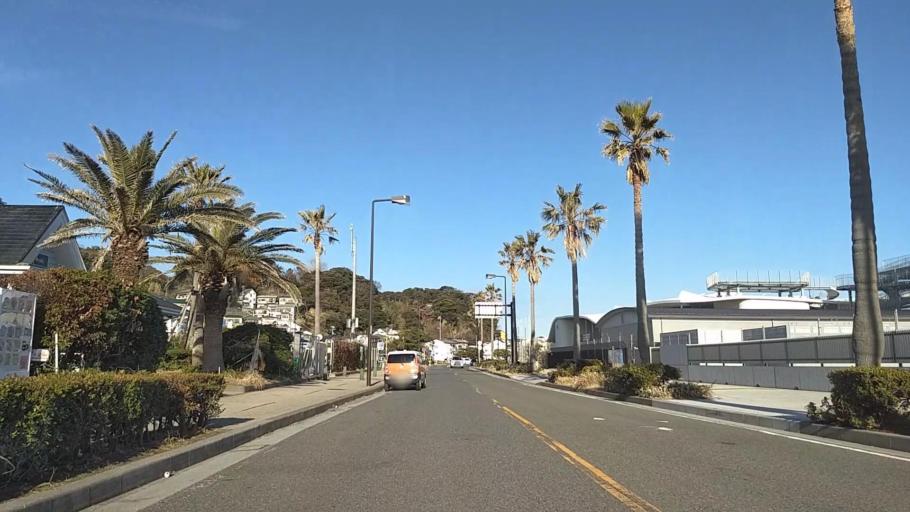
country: JP
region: Kanagawa
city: Fujisawa
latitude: 35.2986
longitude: 139.4840
